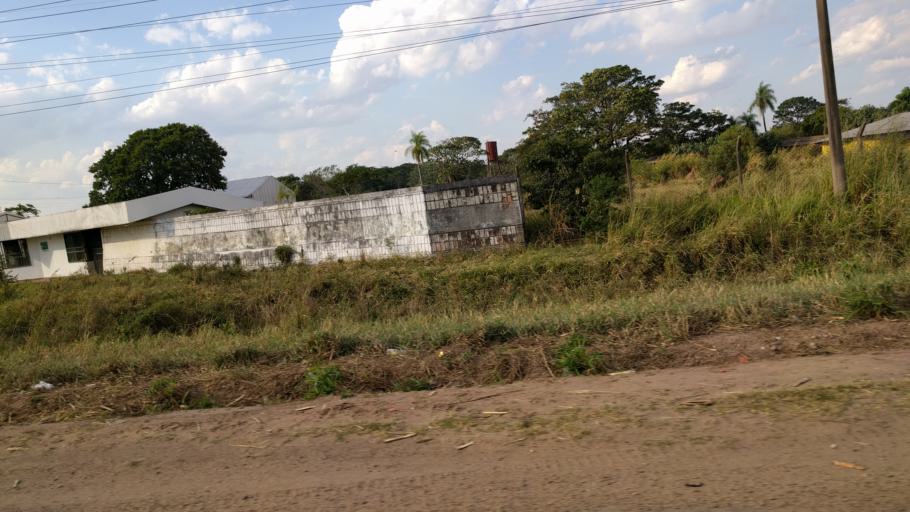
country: BO
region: Santa Cruz
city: Montero
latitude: -17.3731
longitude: -63.2331
